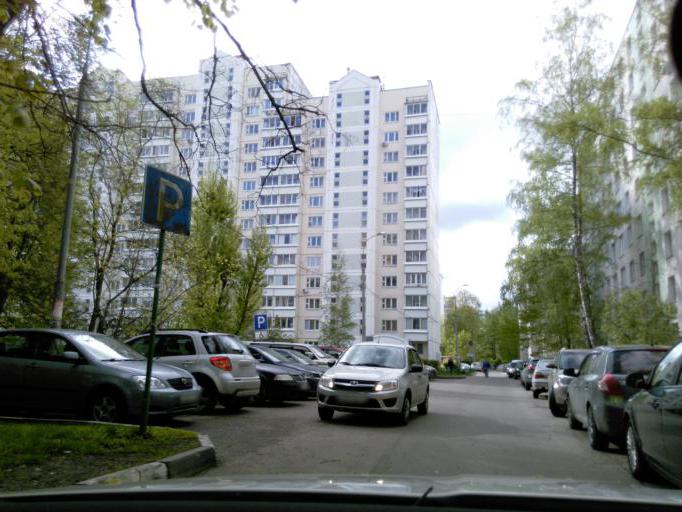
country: RU
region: Moskovskaya
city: Mendeleyevo
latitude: 55.9996
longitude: 37.2115
